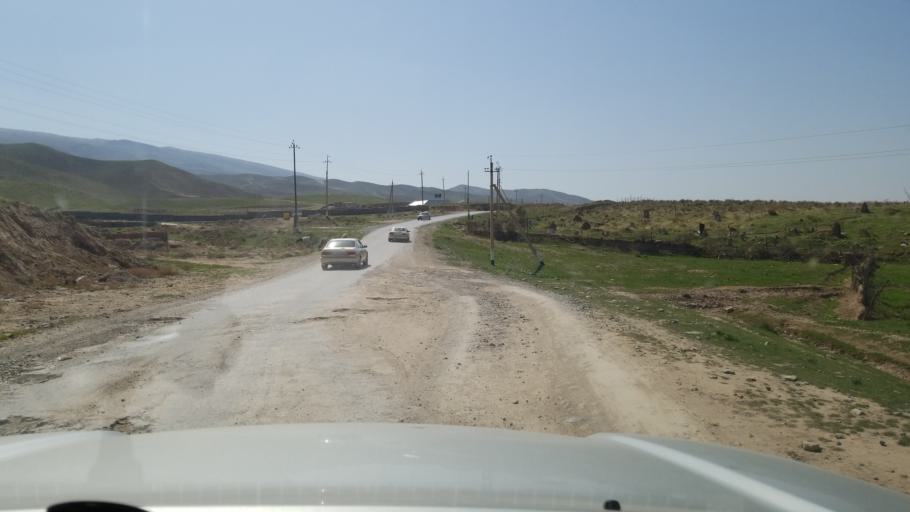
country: TM
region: Lebap
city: Gowurdak
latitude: 37.8792
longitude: 66.4548
